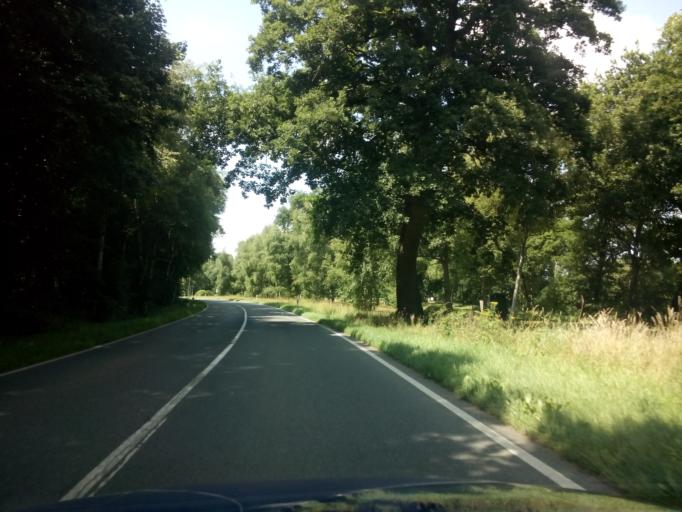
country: DE
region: Lower Saxony
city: Worpswede
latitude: 53.2649
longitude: 8.9065
